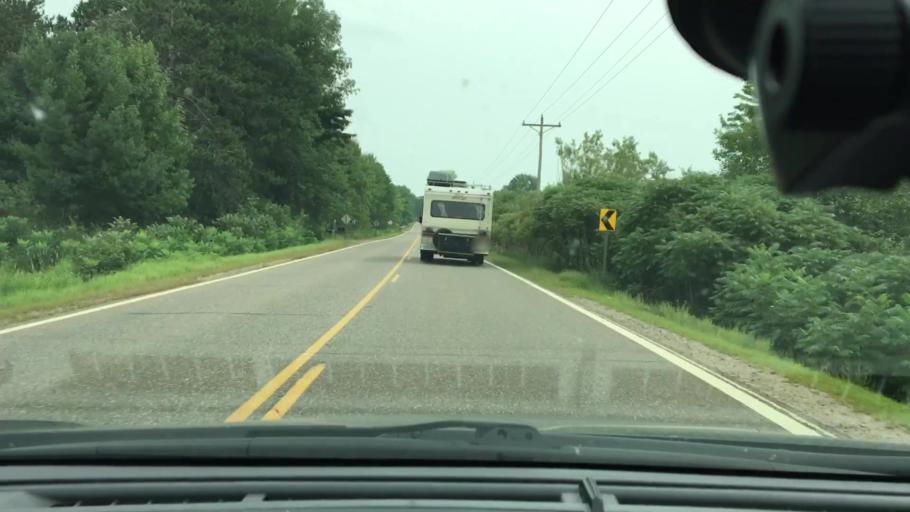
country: US
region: Minnesota
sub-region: Aitkin County
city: Aitkin
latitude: 46.4009
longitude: -93.7687
